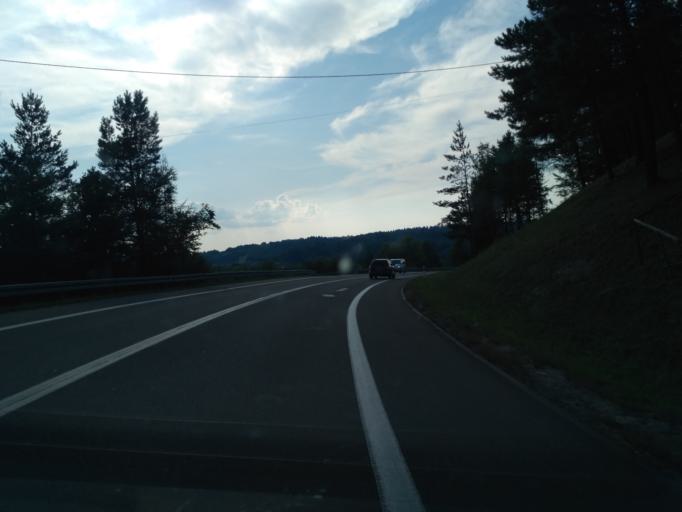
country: PL
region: Subcarpathian Voivodeship
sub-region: Powiat leski
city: Uherce Mineralne
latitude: 49.4703
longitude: 22.4209
